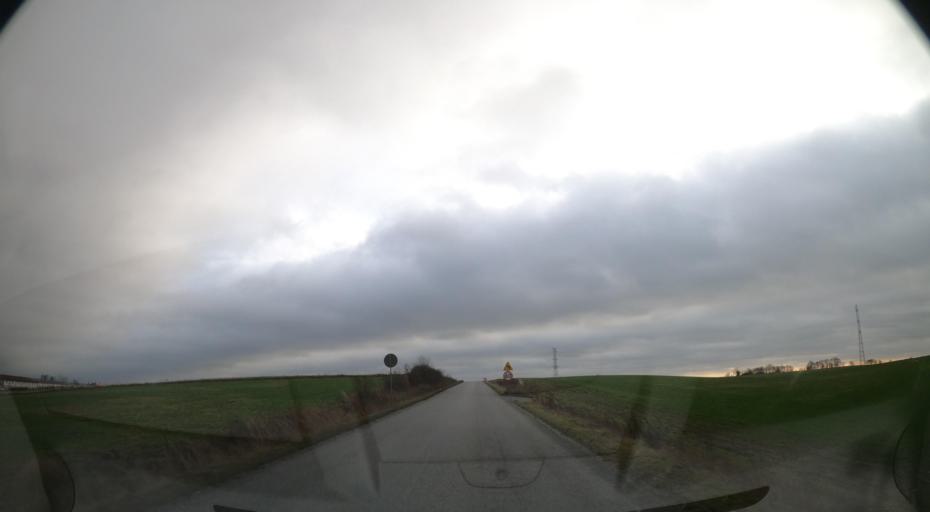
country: PL
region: Kujawsko-Pomorskie
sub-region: Powiat nakielski
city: Sadki
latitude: 53.1829
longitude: 17.4038
